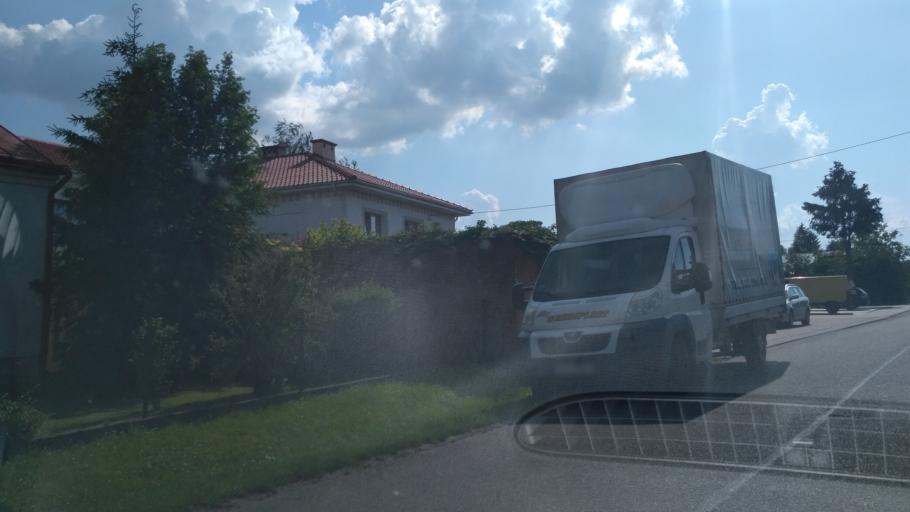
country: PL
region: Subcarpathian Voivodeship
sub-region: Powiat jaroslawski
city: Ostrow
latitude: 49.9403
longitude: 22.7444
